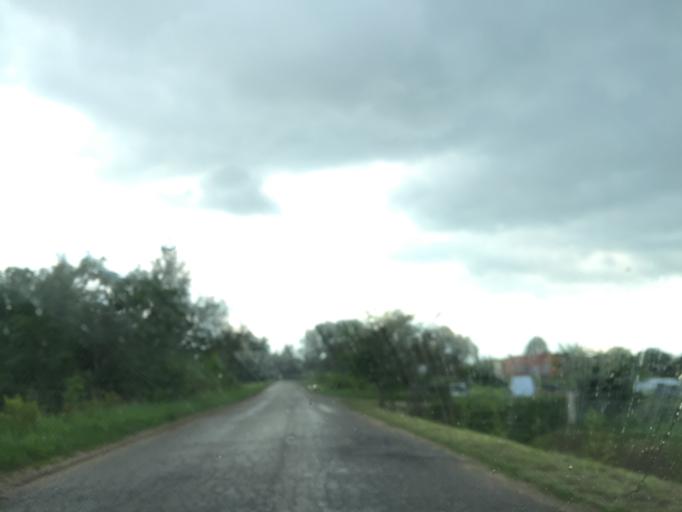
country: LV
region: Dobeles Rajons
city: Dobele
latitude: 56.6232
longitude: 23.3478
